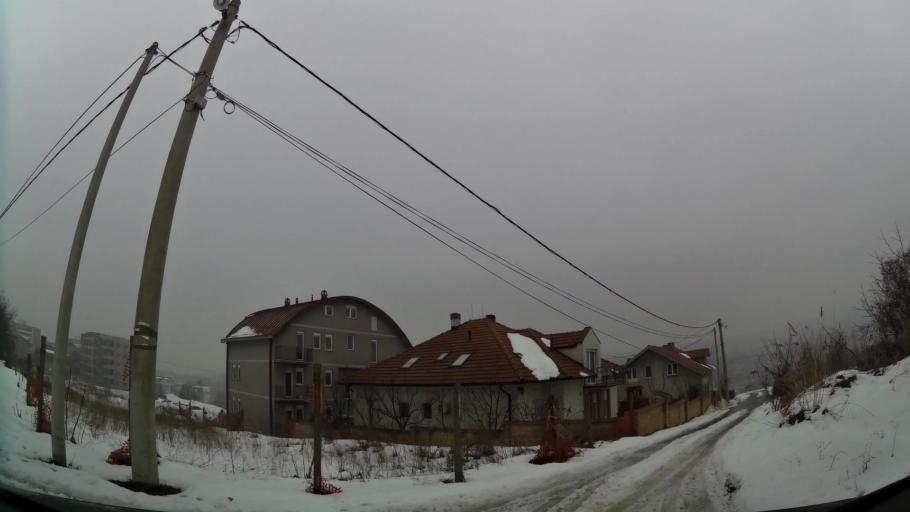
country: RS
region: Central Serbia
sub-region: Belgrade
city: Zvezdara
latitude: 44.7842
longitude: 20.5325
